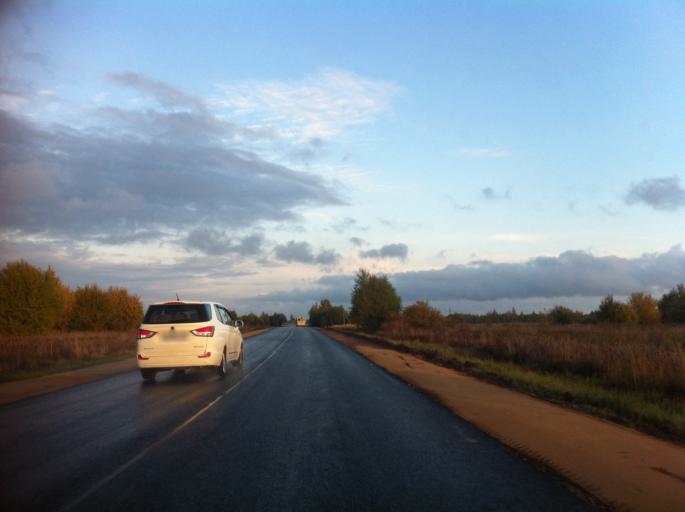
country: RU
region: Pskov
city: Izborsk
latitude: 57.8394
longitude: 28.0275
